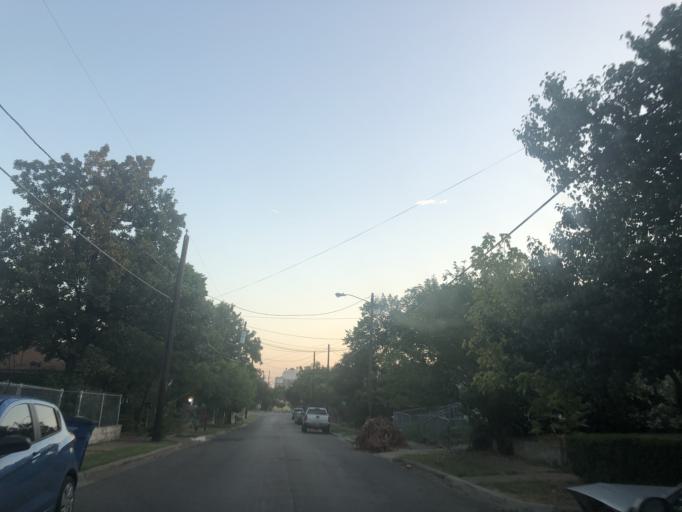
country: US
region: Texas
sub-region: Dallas County
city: Dallas
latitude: 32.7516
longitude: -96.8192
